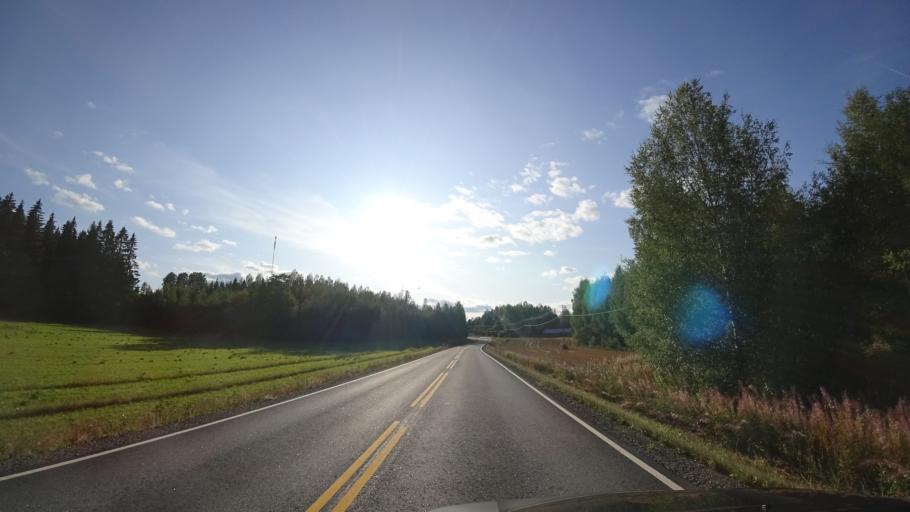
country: FI
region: Paijanne Tavastia
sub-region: Lahti
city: Hollola
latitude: 61.1441
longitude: 25.3435
